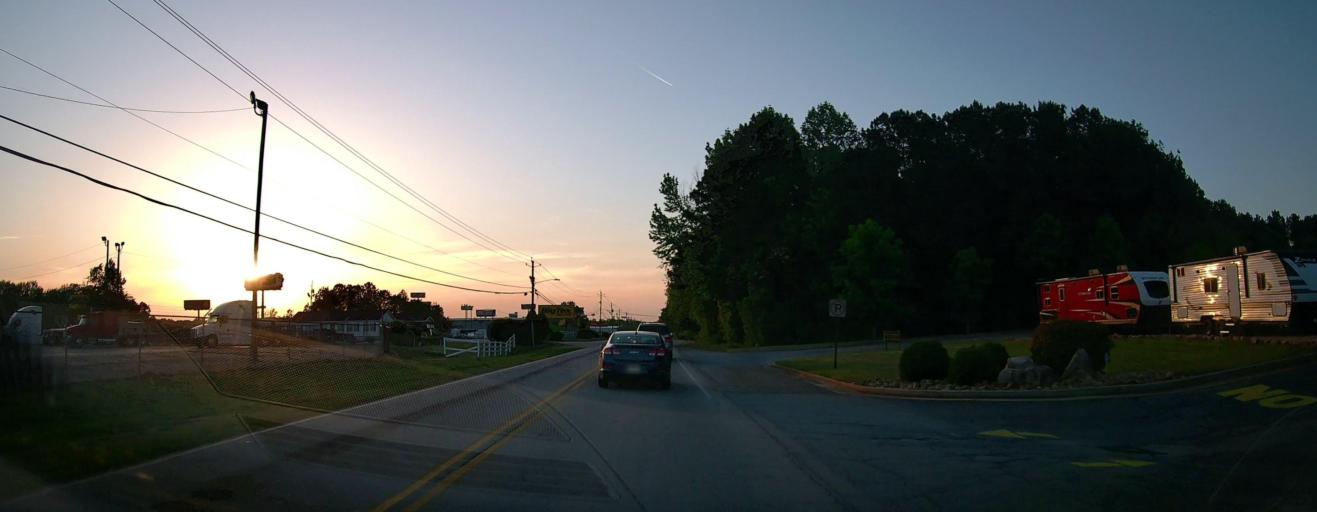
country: US
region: Georgia
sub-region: Henry County
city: McDonough
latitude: 33.4171
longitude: -84.1657
